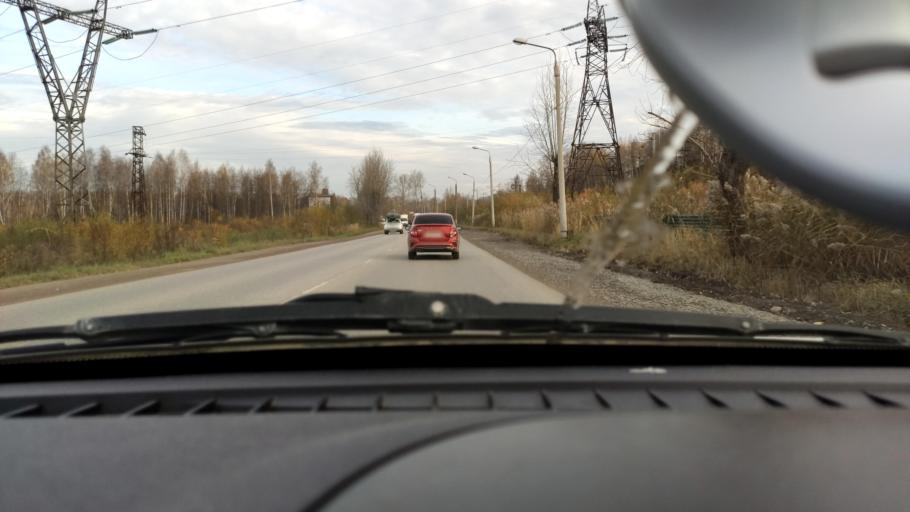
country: RU
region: Perm
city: Perm
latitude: 58.1083
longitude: 56.3627
